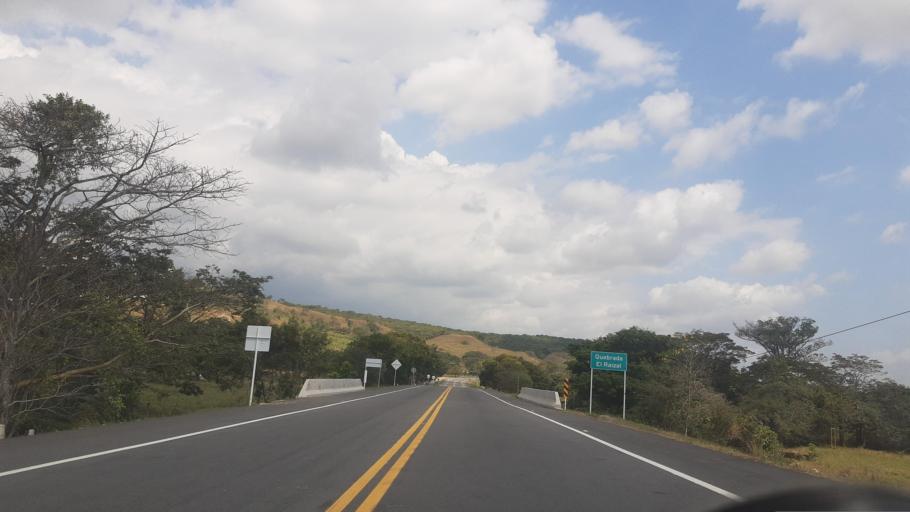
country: CO
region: Casanare
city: Tauramena
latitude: 4.8703
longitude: -72.7051
